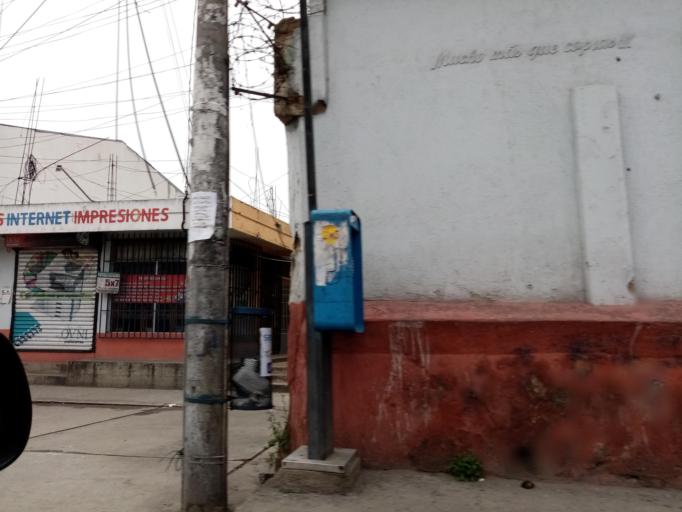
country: GT
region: Quetzaltenango
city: Quetzaltenango
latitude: 14.8406
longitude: -91.5179
